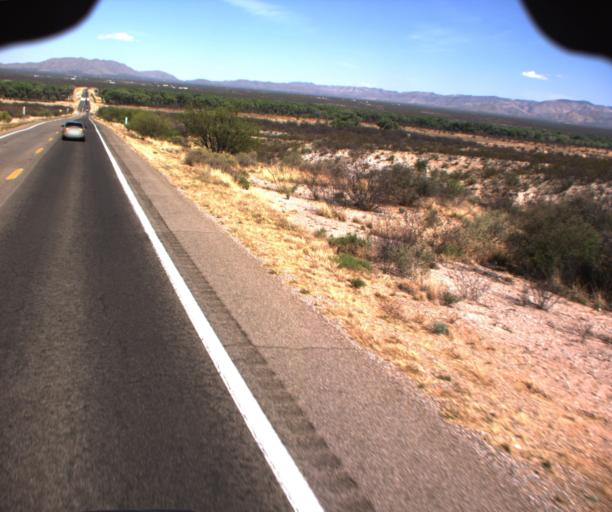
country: US
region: Arizona
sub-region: Cochise County
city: Sierra Vista Southeast
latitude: 31.5481
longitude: -110.1496
